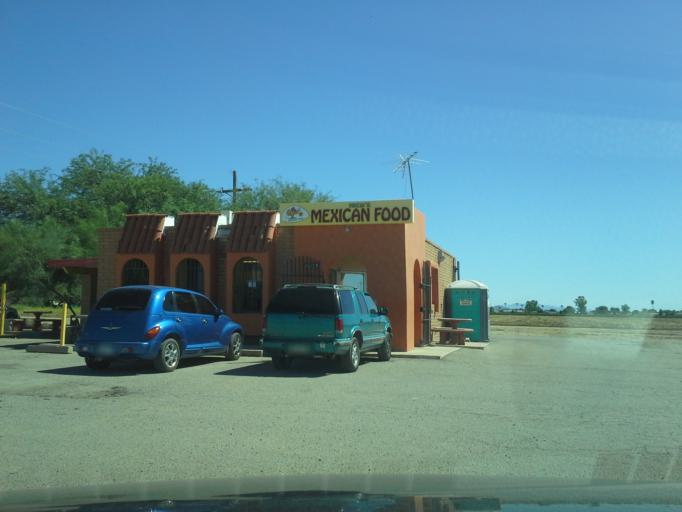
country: US
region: Arizona
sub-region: Pima County
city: Marana
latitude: 32.4602
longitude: -111.2191
